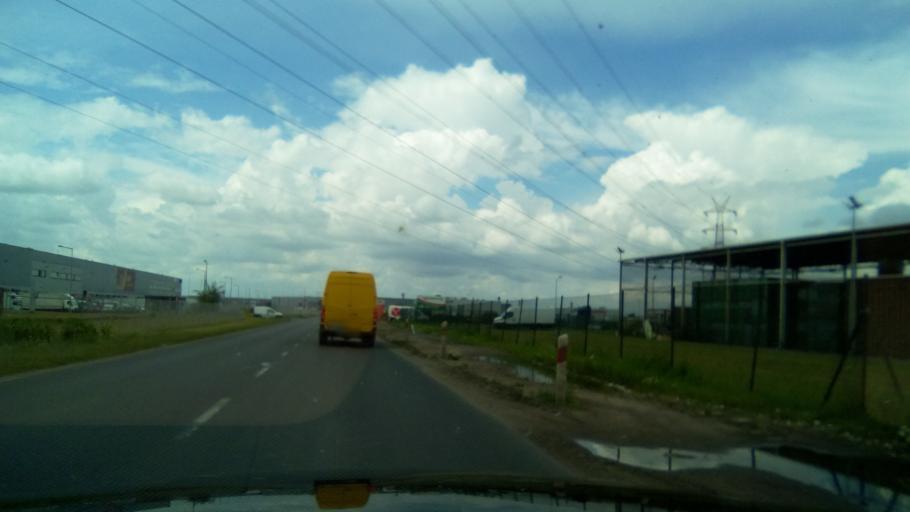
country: PL
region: Greater Poland Voivodeship
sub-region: Powiat poznanski
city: Komorniki
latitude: 52.3465
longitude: 16.8092
